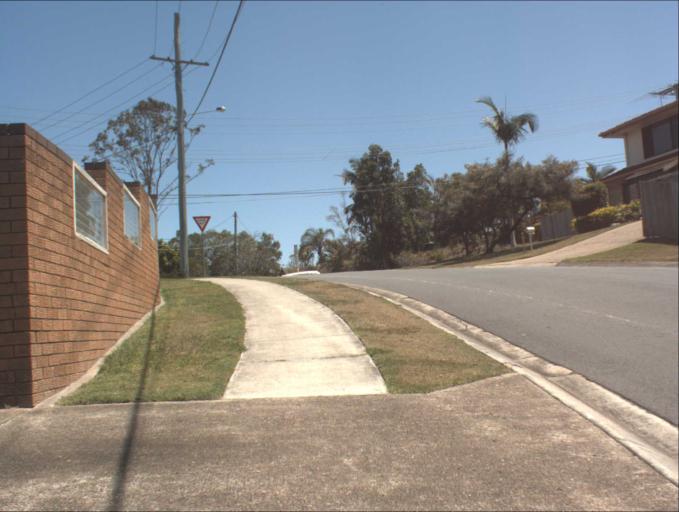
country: AU
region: Queensland
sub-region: Logan
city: Springwood
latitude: -27.6069
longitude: 153.1336
